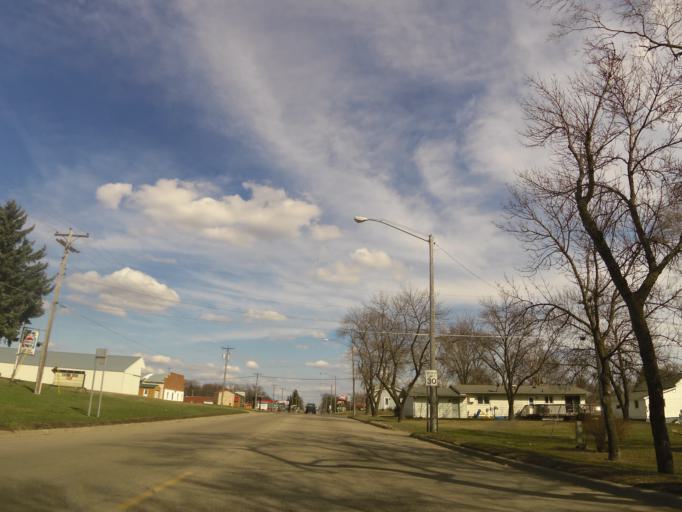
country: US
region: Minnesota
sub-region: Lac qui Parle County
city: Dawson
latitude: 44.9358
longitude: -96.0571
